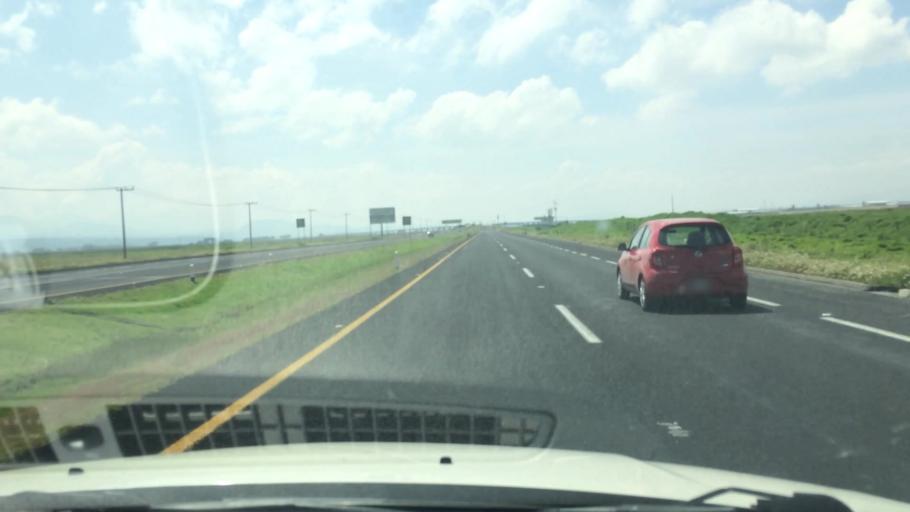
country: MX
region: Mexico
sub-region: Toluca
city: El Cerrillo Vista Hermosa
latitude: 19.3383
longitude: -99.5278
